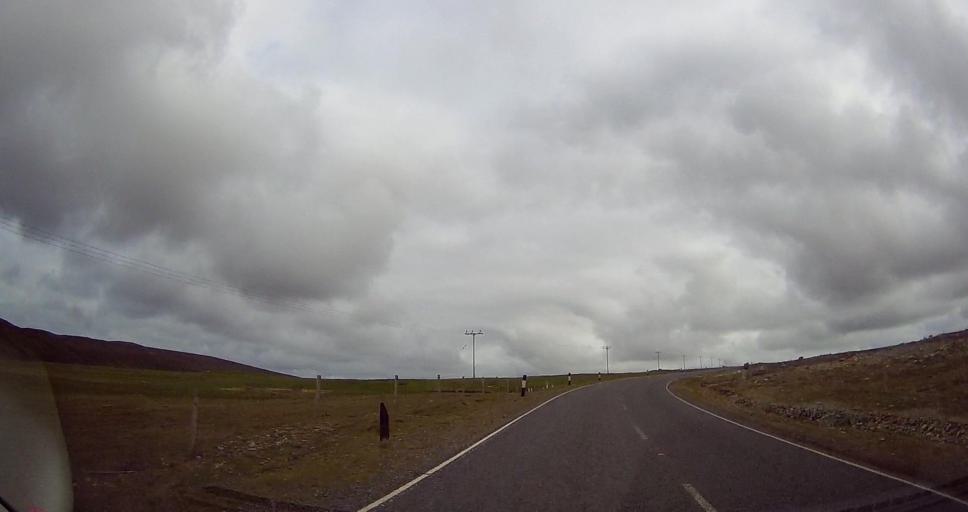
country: GB
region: Scotland
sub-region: Shetland Islands
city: Shetland
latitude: 60.7223
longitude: -0.9093
